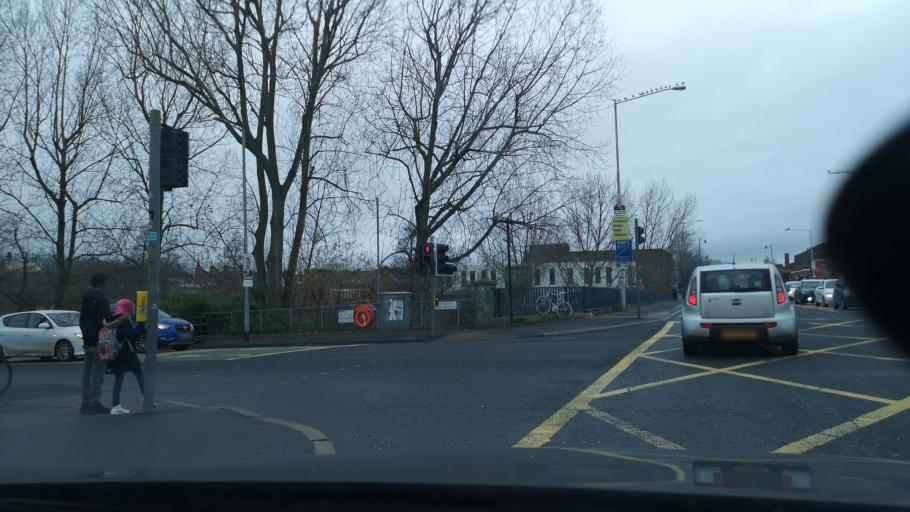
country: GB
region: Northern Ireland
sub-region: City of Belfast
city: Belfast
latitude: 54.5823
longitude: -5.9218
